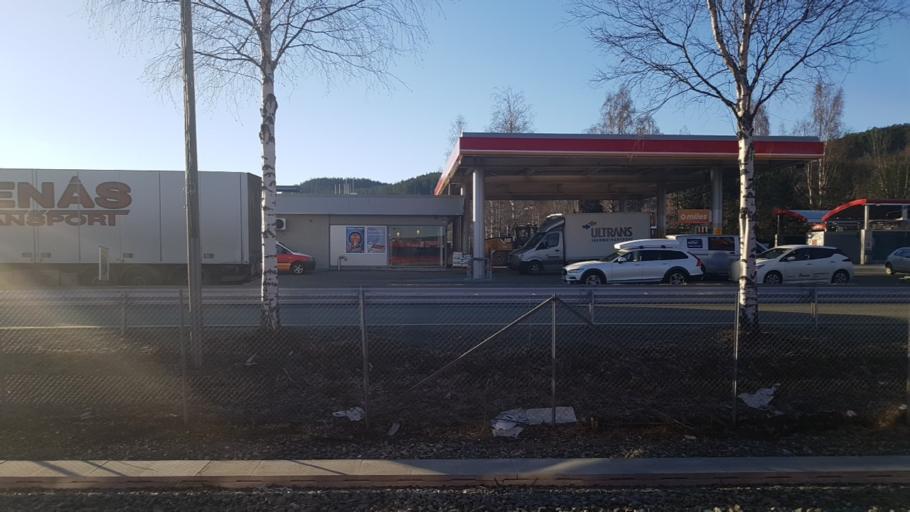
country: NO
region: Sor-Trondelag
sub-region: Malvik
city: Hommelvik
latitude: 63.4132
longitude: 10.7892
